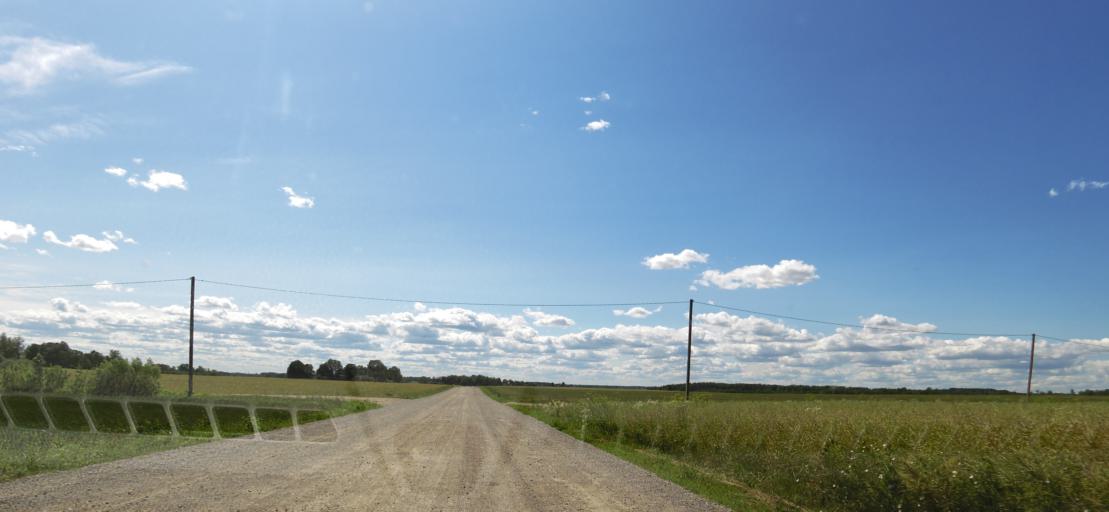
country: LV
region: Bauskas Rajons
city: Bauska
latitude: 56.2464
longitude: 24.2710
